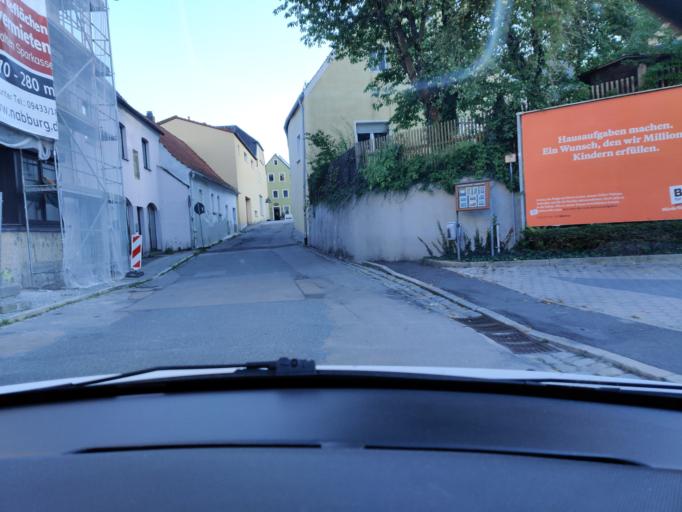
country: DE
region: Bavaria
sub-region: Upper Palatinate
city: Nabburg
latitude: 49.4525
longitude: 12.1800
